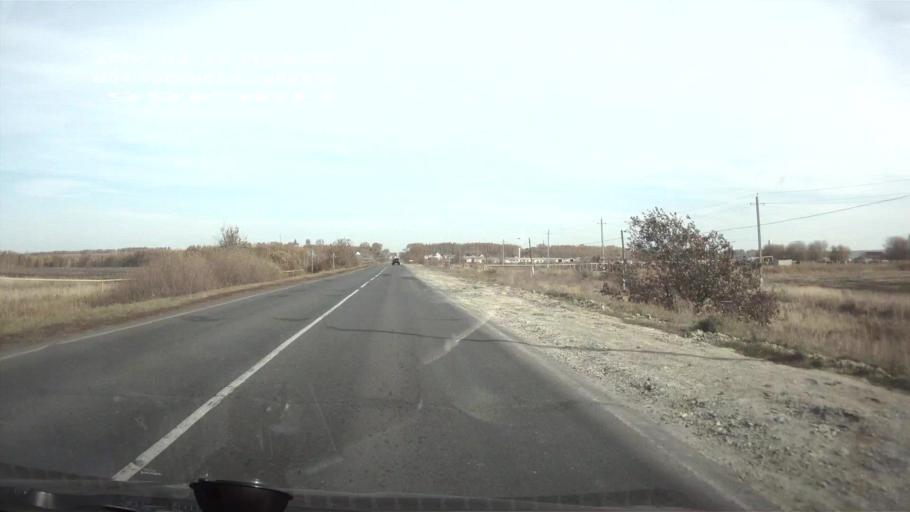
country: RU
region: Mordoviya
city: Atyashevo
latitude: 54.5565
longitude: 45.9691
